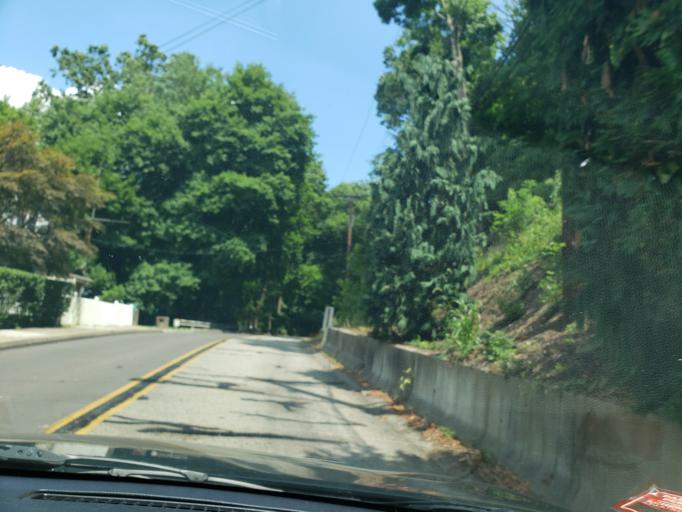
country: US
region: Pennsylvania
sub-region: Allegheny County
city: Coraopolis
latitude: 40.5326
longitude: -80.1686
